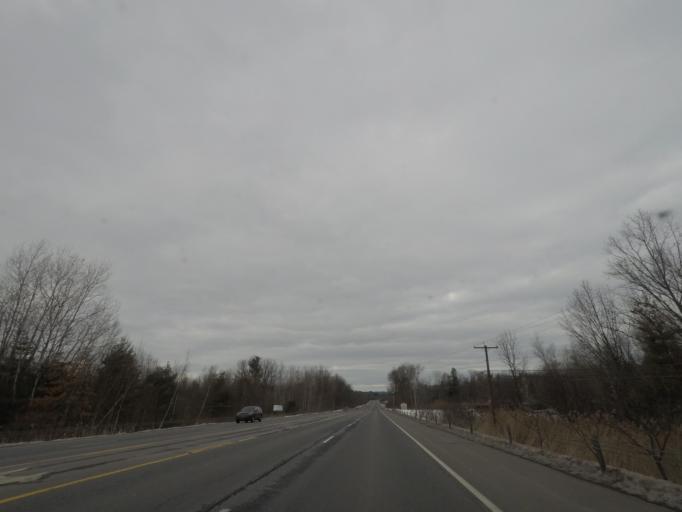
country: US
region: New York
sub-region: Saratoga County
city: Country Knolls
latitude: 42.9064
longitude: -73.7813
